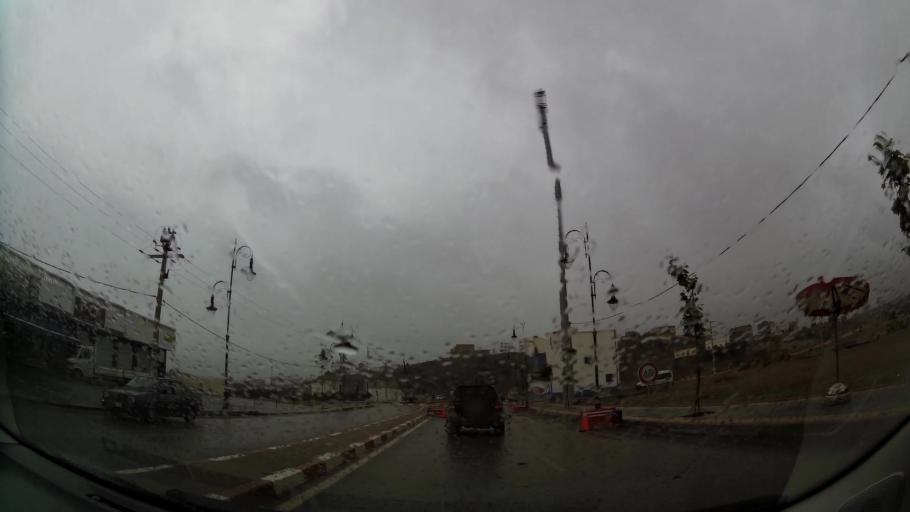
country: MA
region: Taza-Al Hoceima-Taounate
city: Imzourene
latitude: 35.1622
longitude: -3.8551
